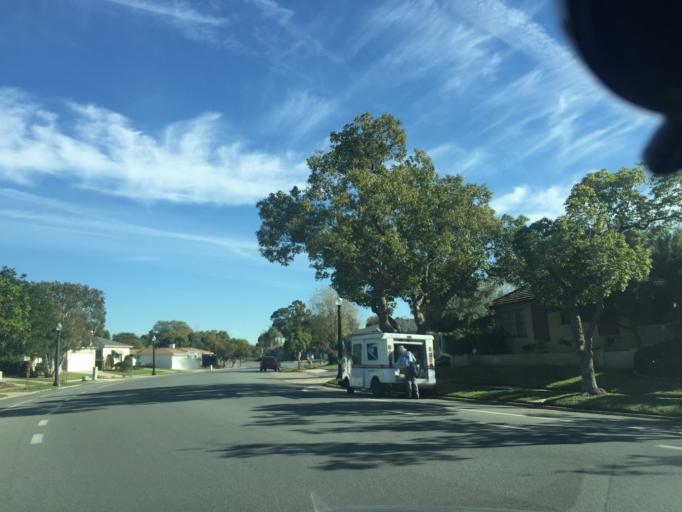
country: US
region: California
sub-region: San Diego County
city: Lemon Grove
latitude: 32.7620
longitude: -117.0913
